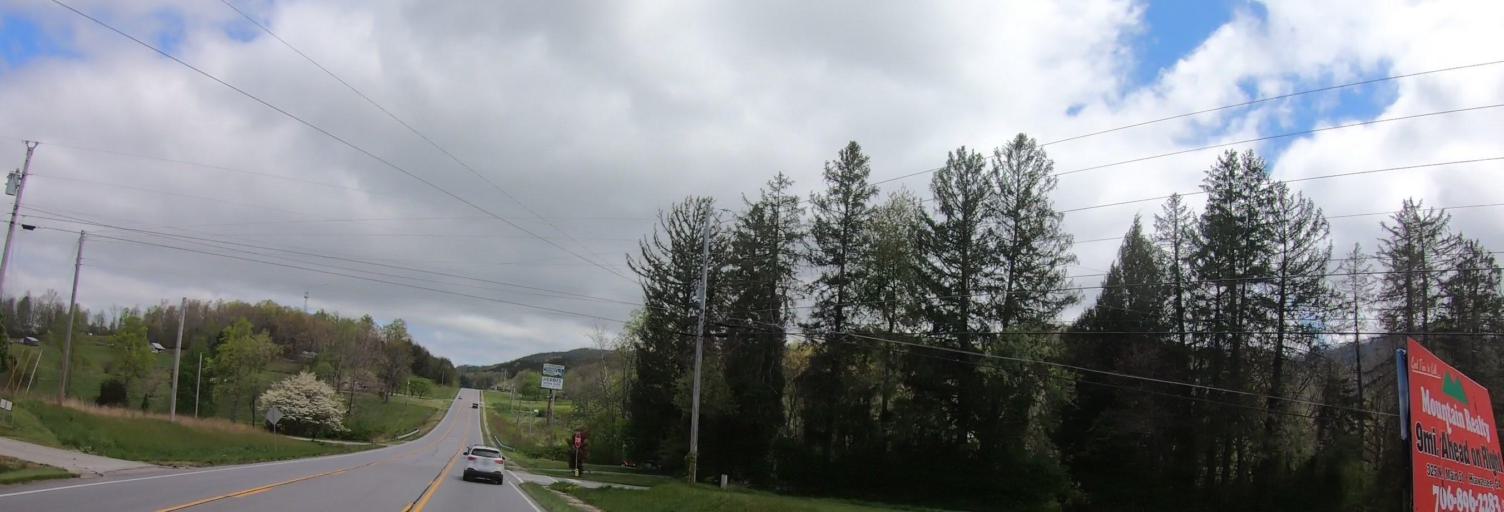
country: US
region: Georgia
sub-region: Towns County
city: Hiawassee
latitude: 34.9198
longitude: -83.8560
